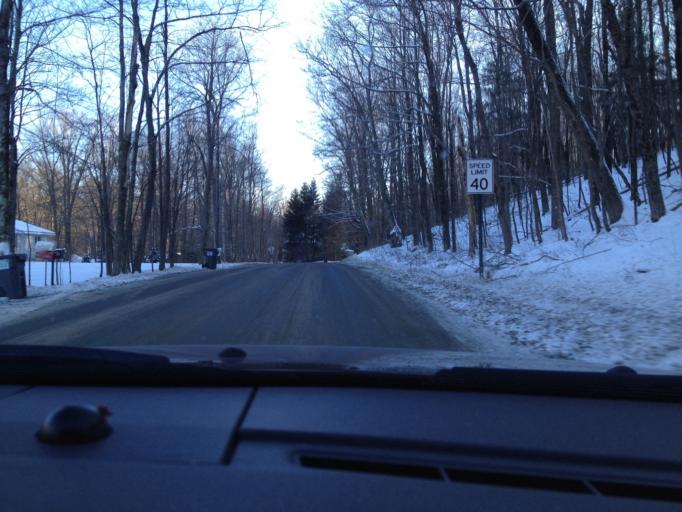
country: US
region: New York
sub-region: Rensselaer County
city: Averill Park
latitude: 42.6241
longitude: -73.5762
